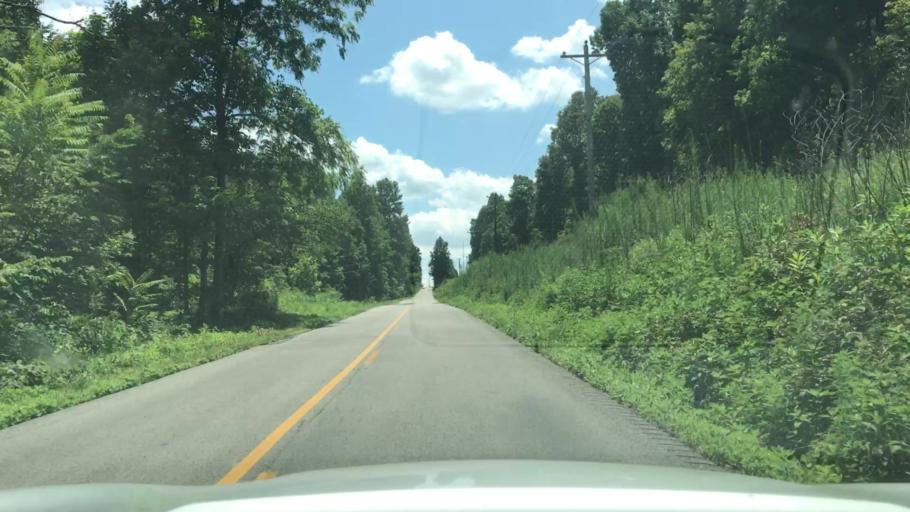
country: US
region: Kentucky
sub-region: Hopkins County
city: Nortonville
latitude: 37.0424
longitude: -87.3492
